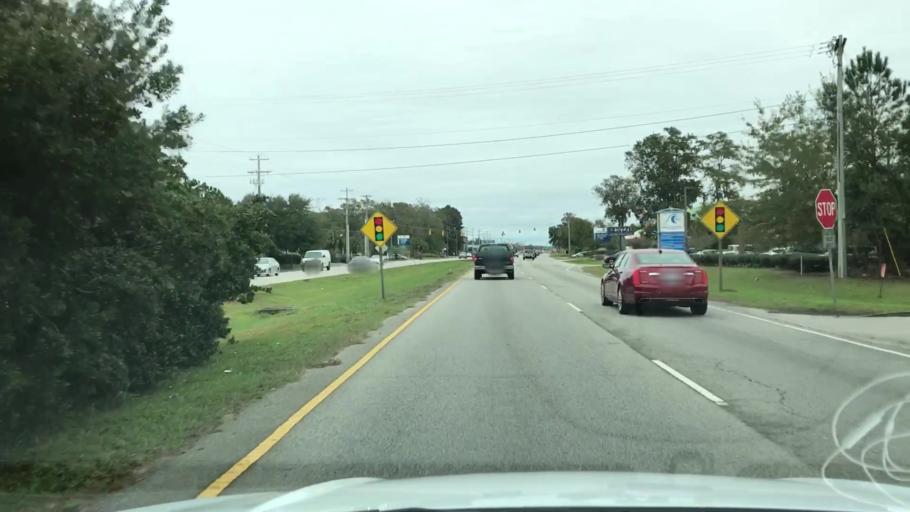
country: US
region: South Carolina
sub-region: Georgetown County
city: Murrells Inlet
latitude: 33.5573
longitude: -79.0431
